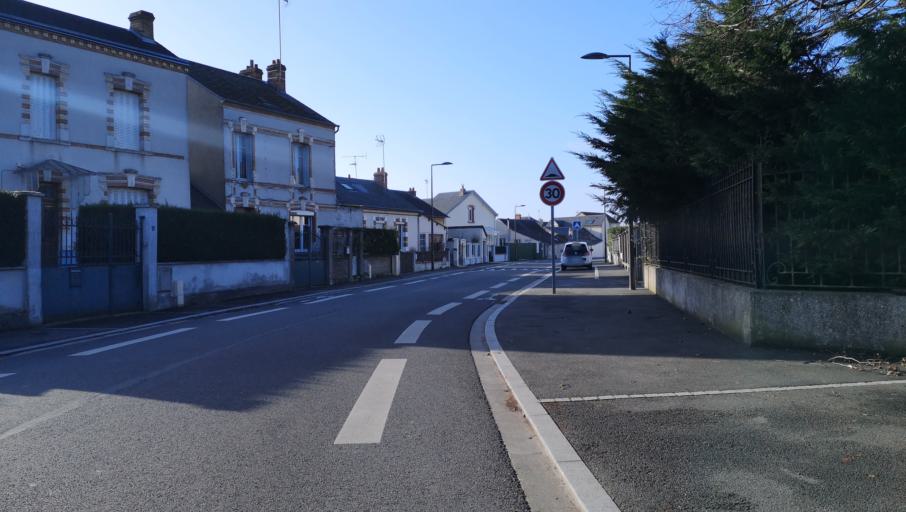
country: FR
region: Centre
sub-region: Departement du Loiret
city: Orleans
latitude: 47.8861
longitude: 1.8944
